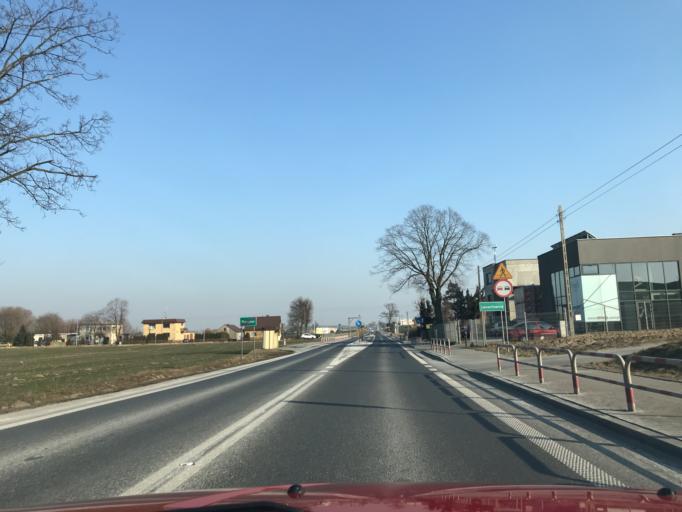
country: PL
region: Greater Poland Voivodeship
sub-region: Powiat pleszewski
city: Pleszew
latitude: 51.8933
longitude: 17.8209
